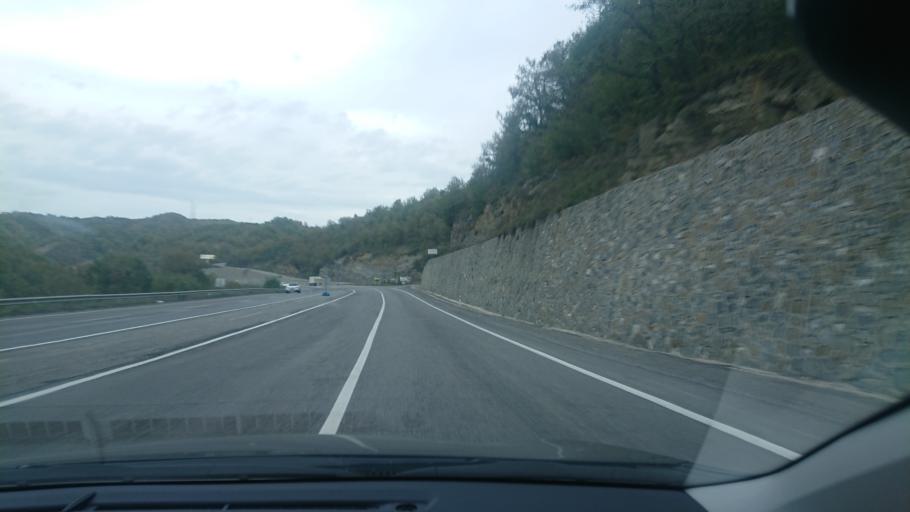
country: TR
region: Zonguldak
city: Beycuma
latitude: 41.4048
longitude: 31.9367
